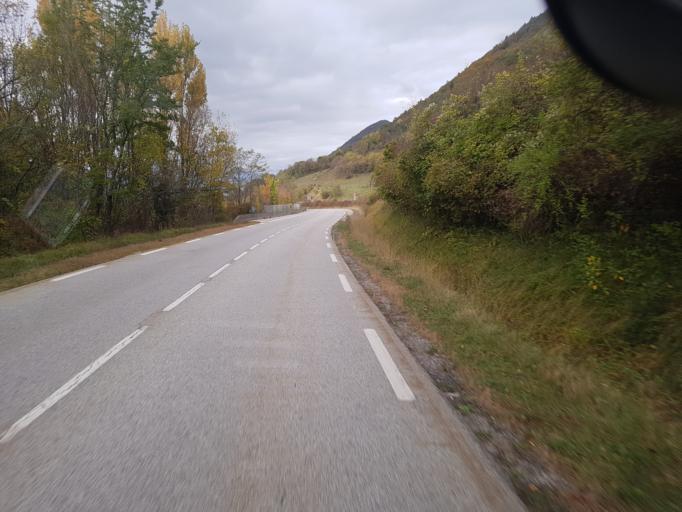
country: FR
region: Rhone-Alpes
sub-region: Departement de l'Isere
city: Vif
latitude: 45.0171
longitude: 5.6590
